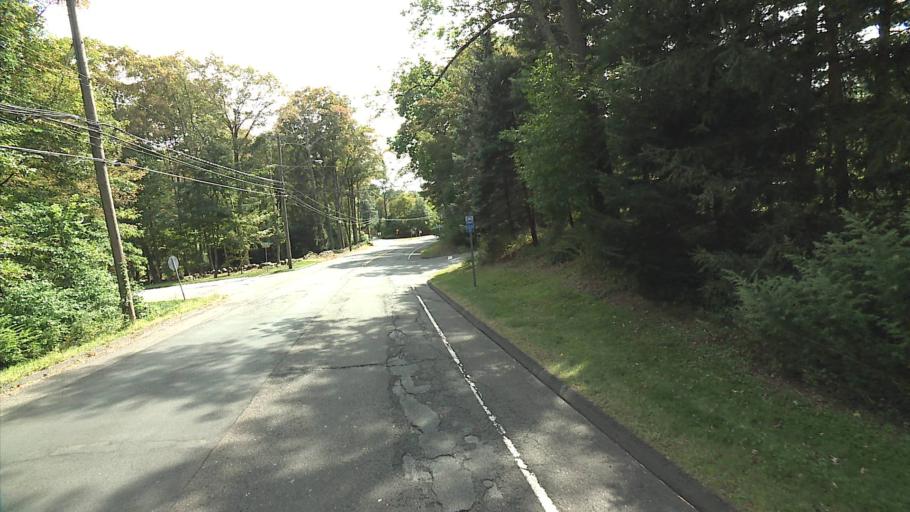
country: US
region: Connecticut
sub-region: Fairfield County
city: North Stamford
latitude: 41.1418
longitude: -73.5459
